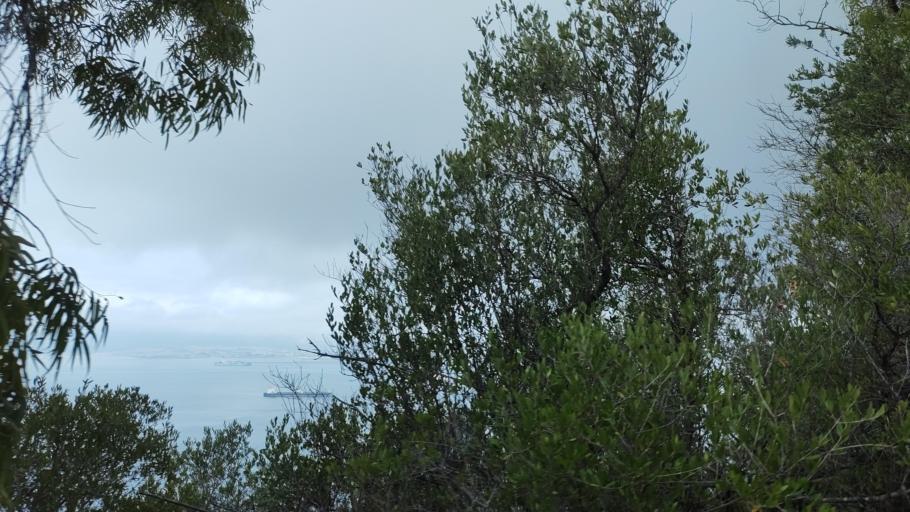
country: GI
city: Gibraltar
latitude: 36.1226
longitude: -5.3463
